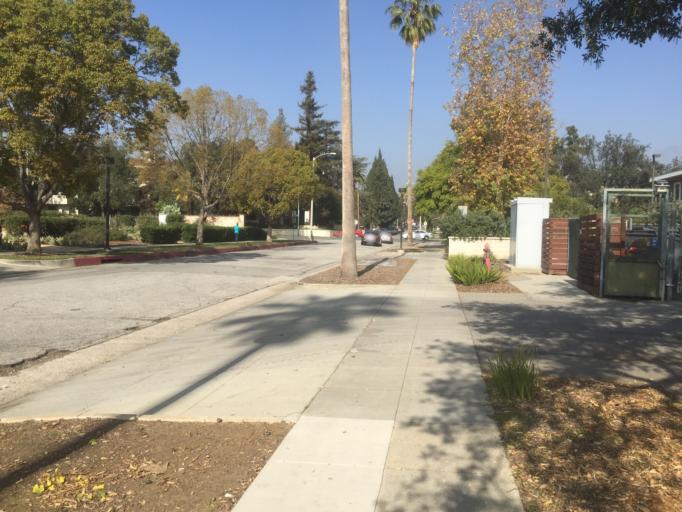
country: US
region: California
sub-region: Los Angeles County
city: Pasadena
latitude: 34.1407
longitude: -118.1228
